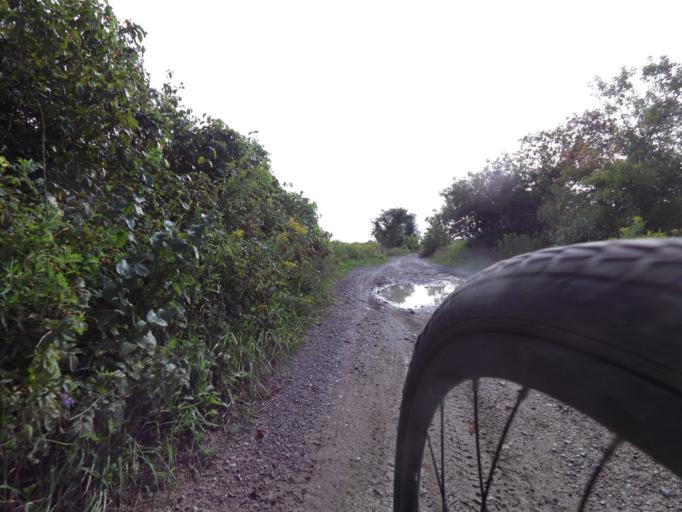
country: CA
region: Ontario
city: Quinte West
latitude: 44.0500
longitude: -77.6166
